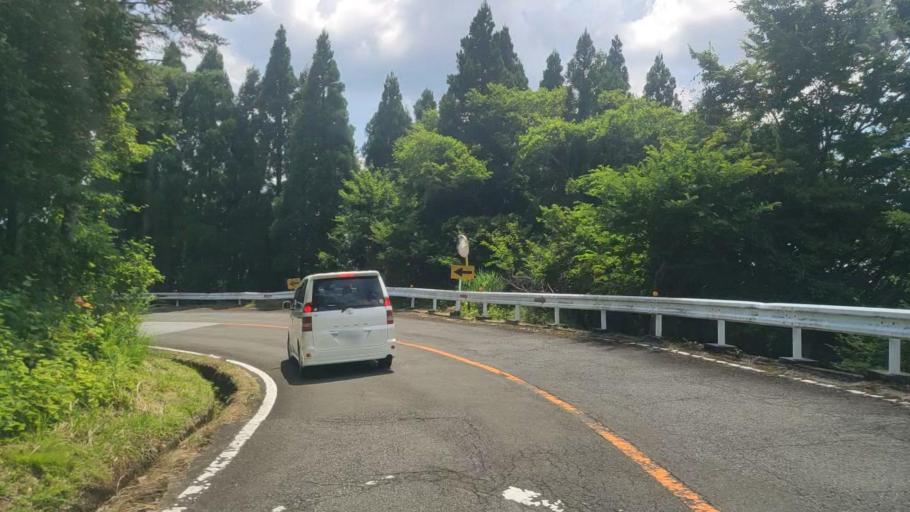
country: JP
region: Gifu
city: Tarui
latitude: 35.3914
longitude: 136.4318
